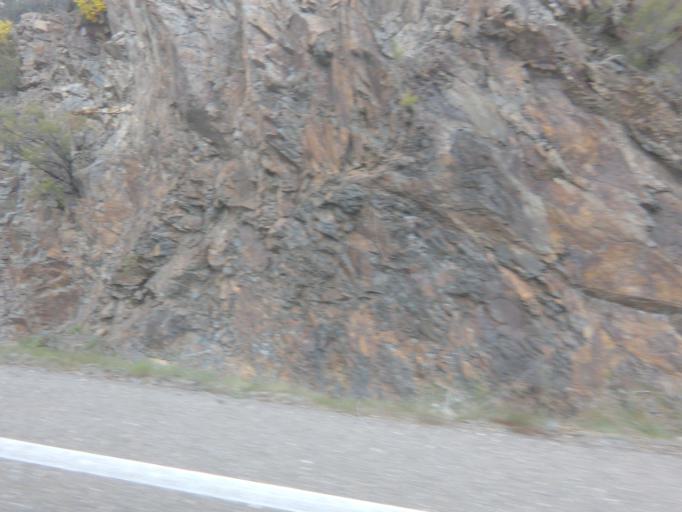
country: ES
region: Extremadura
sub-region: Provincia de Caceres
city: Acebo
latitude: 40.2382
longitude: -6.6871
